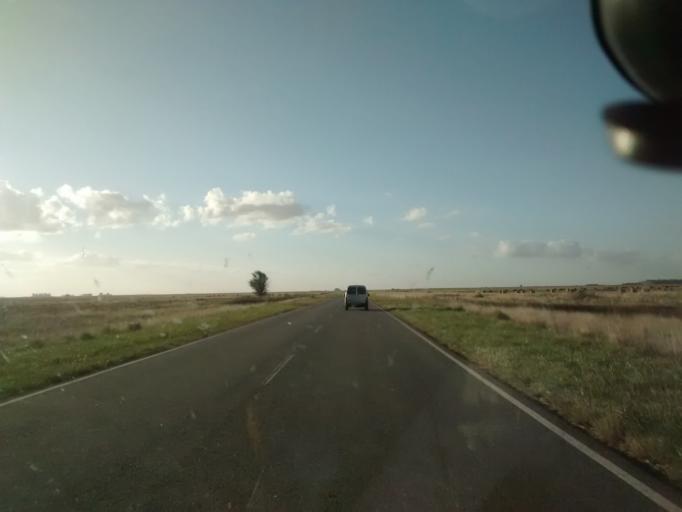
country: AR
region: Buenos Aires
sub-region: Partido de General Belgrano
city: General Belgrano
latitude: -36.0832
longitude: -58.6162
